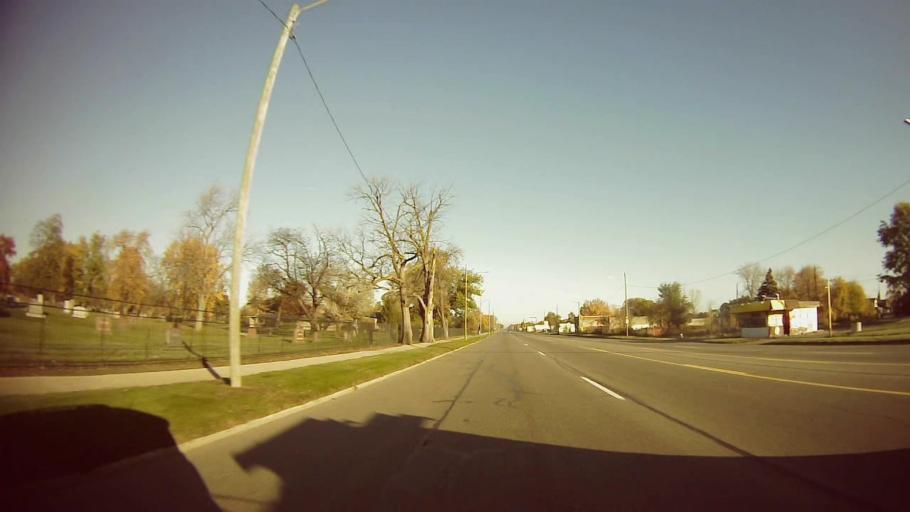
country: US
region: Michigan
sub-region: Wayne County
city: Hamtramck
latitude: 42.4095
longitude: -83.0234
